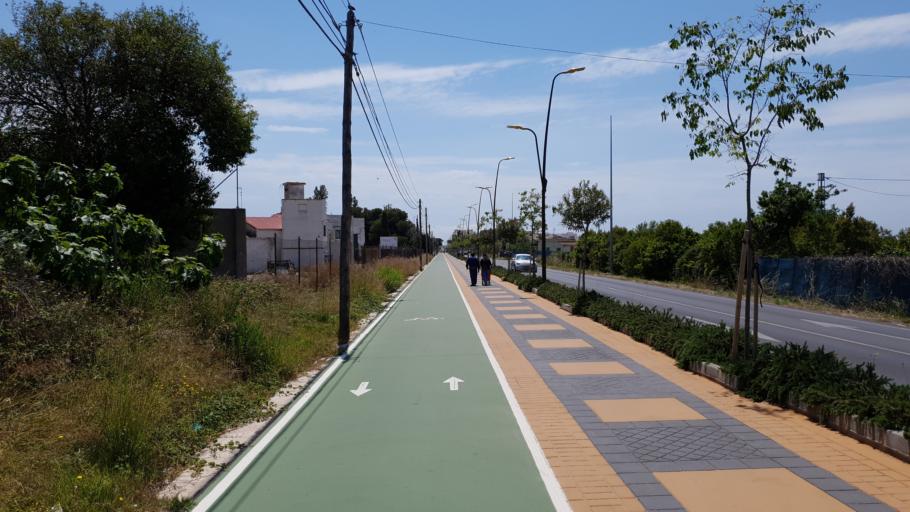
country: ES
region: Valencia
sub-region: Provincia de Castello
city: Burriana
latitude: 39.8754
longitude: -0.0767
